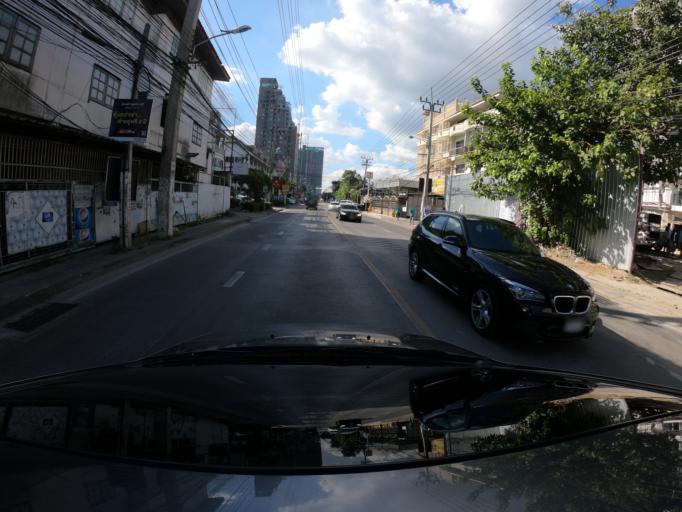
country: TH
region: Bangkok
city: Bang Na
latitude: 13.6567
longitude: 100.6060
